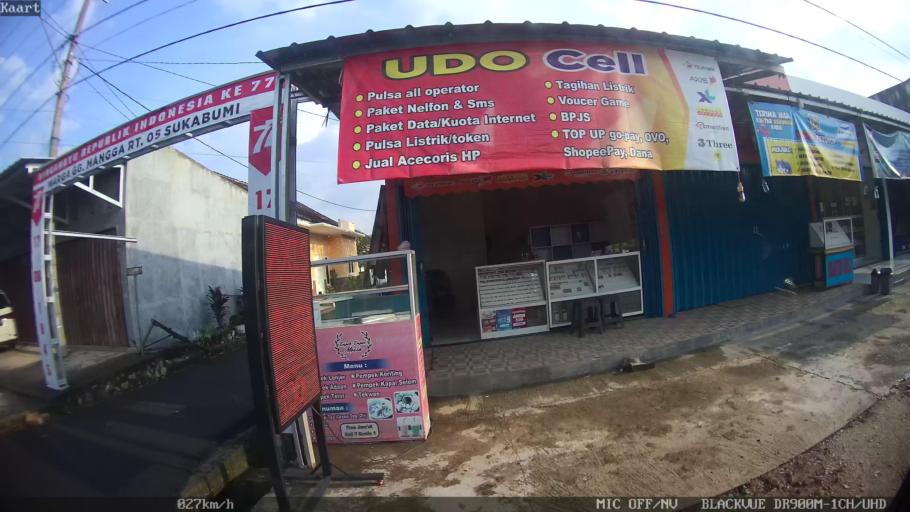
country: ID
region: Lampung
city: Kedaton
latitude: -5.3944
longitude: 105.3101
